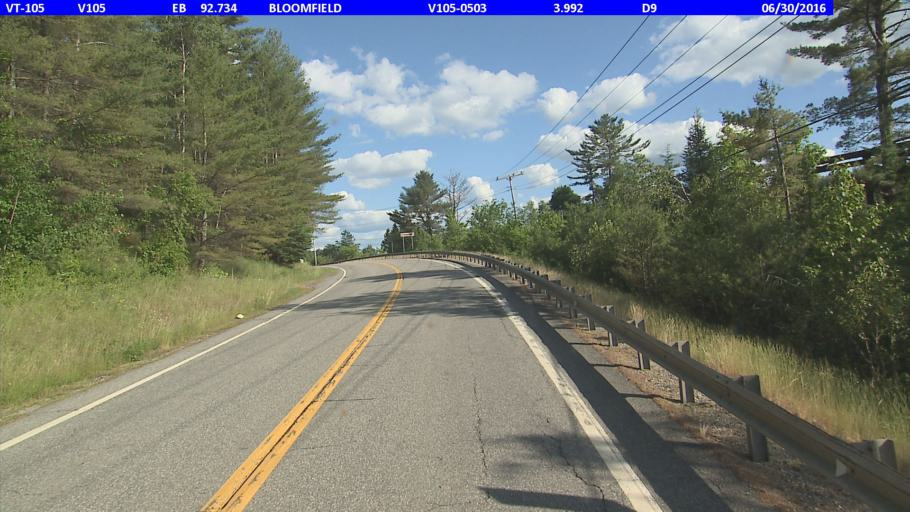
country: US
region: New Hampshire
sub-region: Coos County
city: Stratford
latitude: 44.7552
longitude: -71.6356
